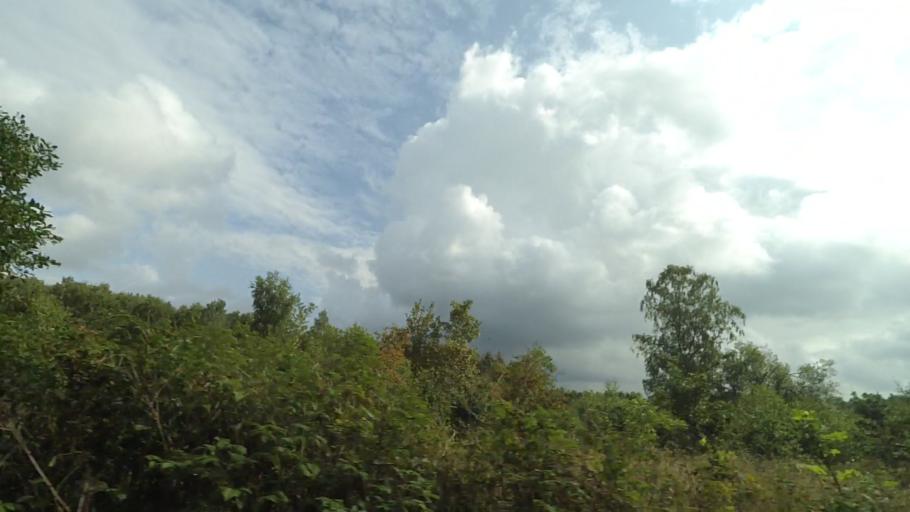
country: DK
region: Central Jutland
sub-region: Syddjurs Kommune
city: Ryomgard
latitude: 56.4570
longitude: 10.5435
